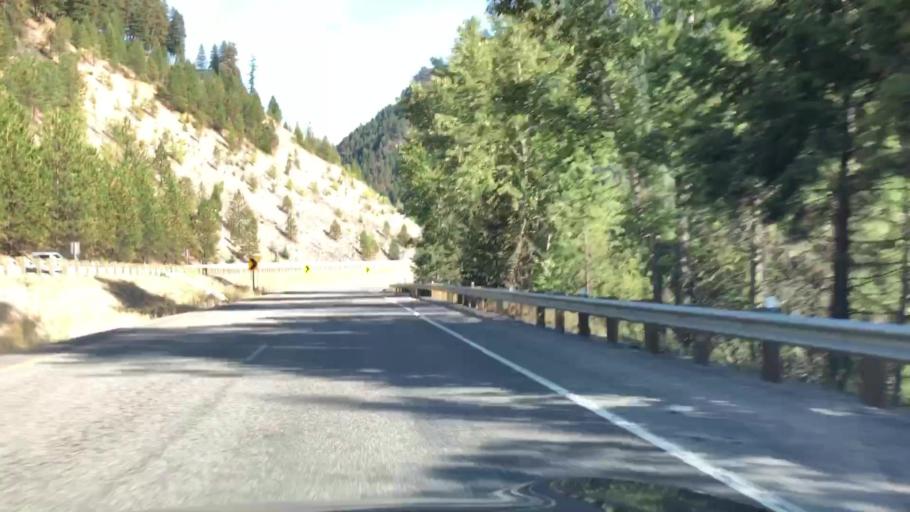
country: US
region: Montana
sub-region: Sanders County
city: Thompson Falls
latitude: 47.3151
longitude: -115.2384
